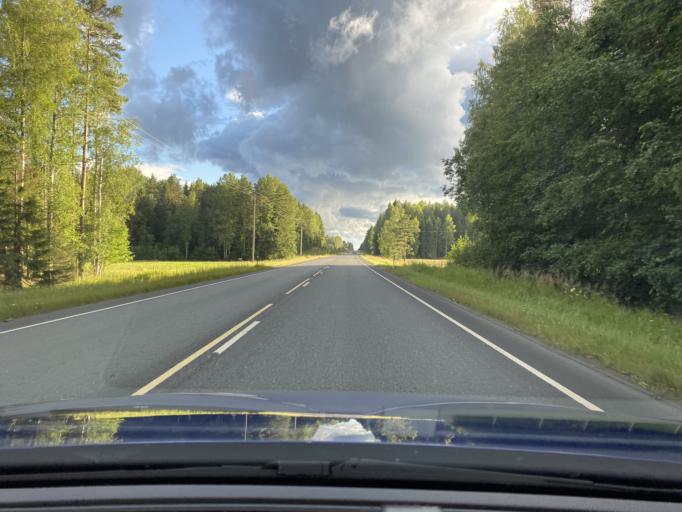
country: FI
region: Haeme
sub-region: Haemeenlinna
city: Renko
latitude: 60.8719
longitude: 24.2127
